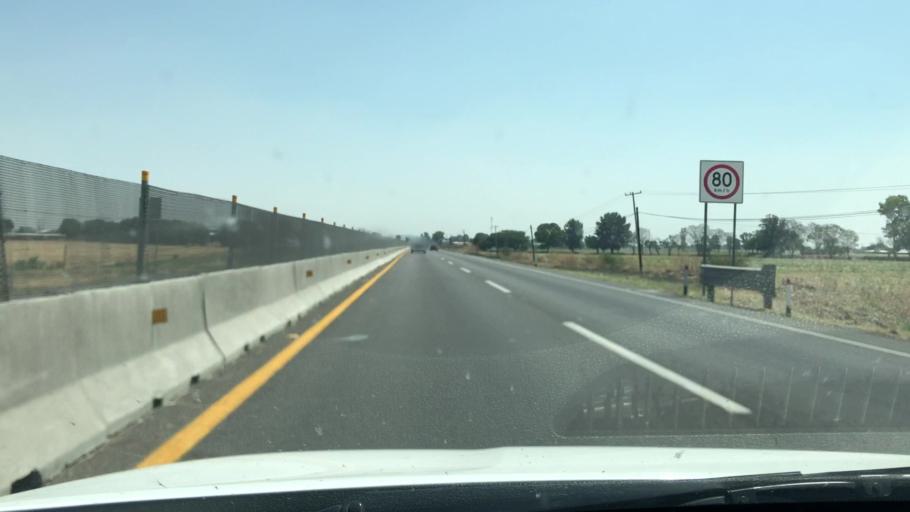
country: MX
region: Guanajuato
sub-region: Abasolo
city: San Bernardo Pena Blanca
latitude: 20.4823
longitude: -101.4945
